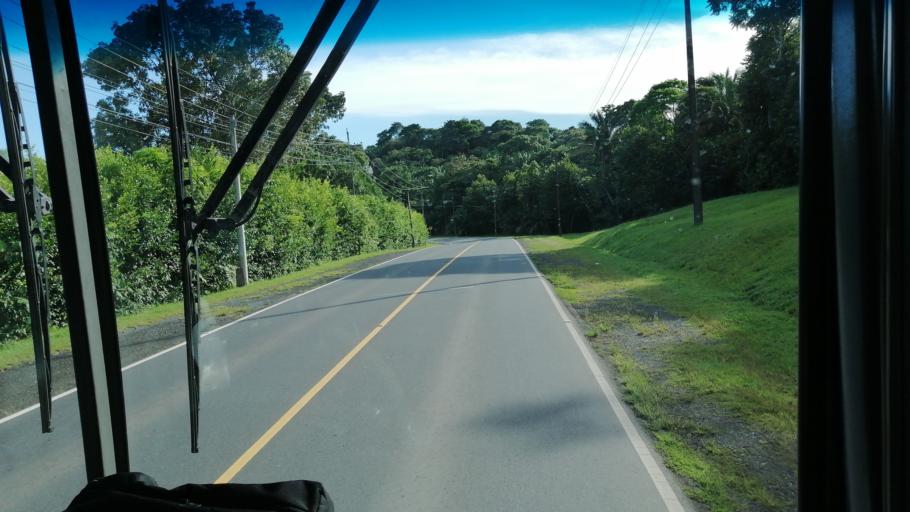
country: PA
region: Panama
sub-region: Distrito de Panama
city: Ancon
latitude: 8.9472
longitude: -79.5911
